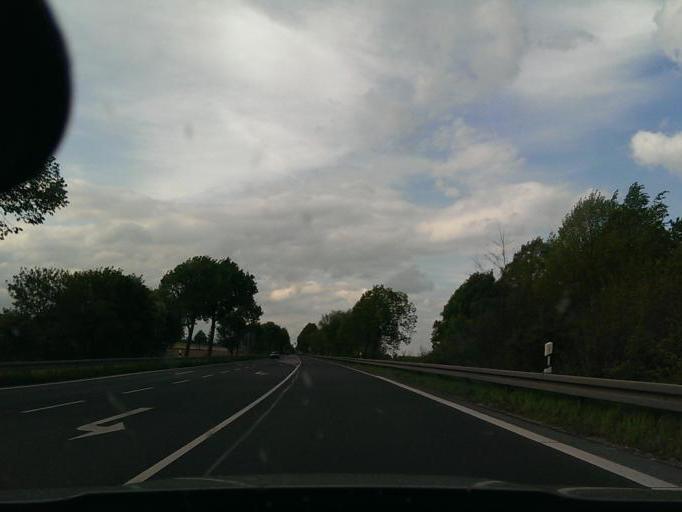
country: DE
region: Lower Saxony
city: Elze
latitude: 52.1347
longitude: 9.7315
